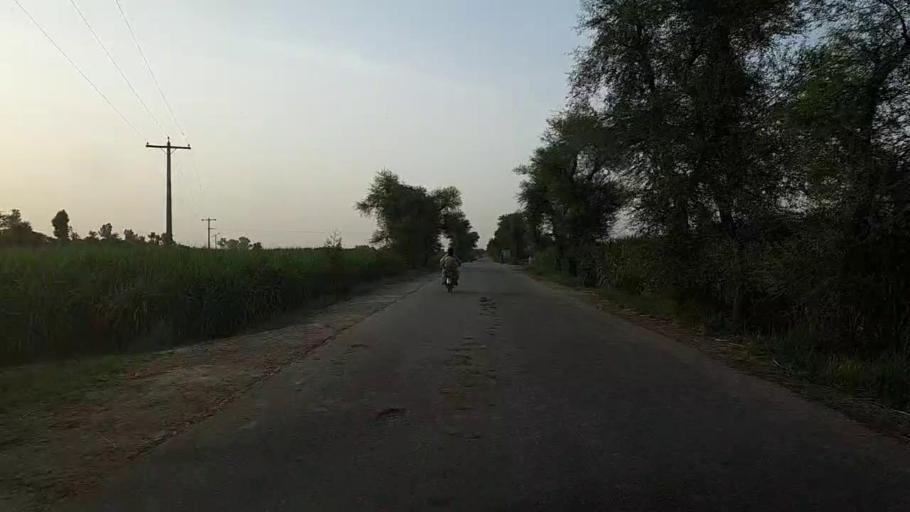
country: PK
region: Sindh
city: Ubauro
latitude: 28.2234
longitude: 69.8192
